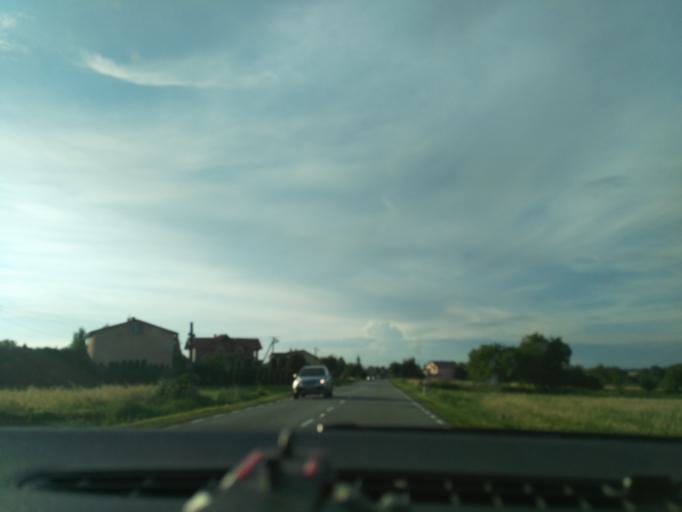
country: PL
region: Lublin Voivodeship
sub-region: Powiat krasnicki
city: Szastarka
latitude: 50.8199
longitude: 22.3161
